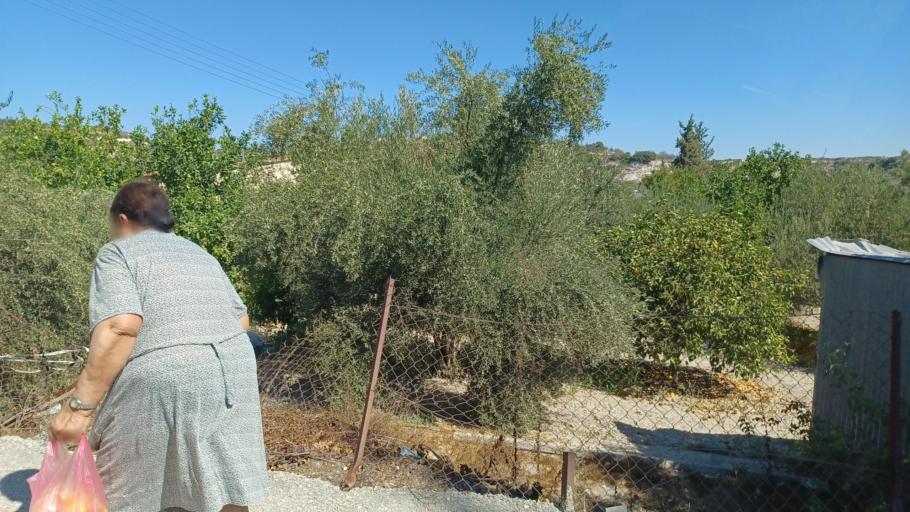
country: CY
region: Pafos
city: Mesogi
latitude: 34.8548
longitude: 32.5128
